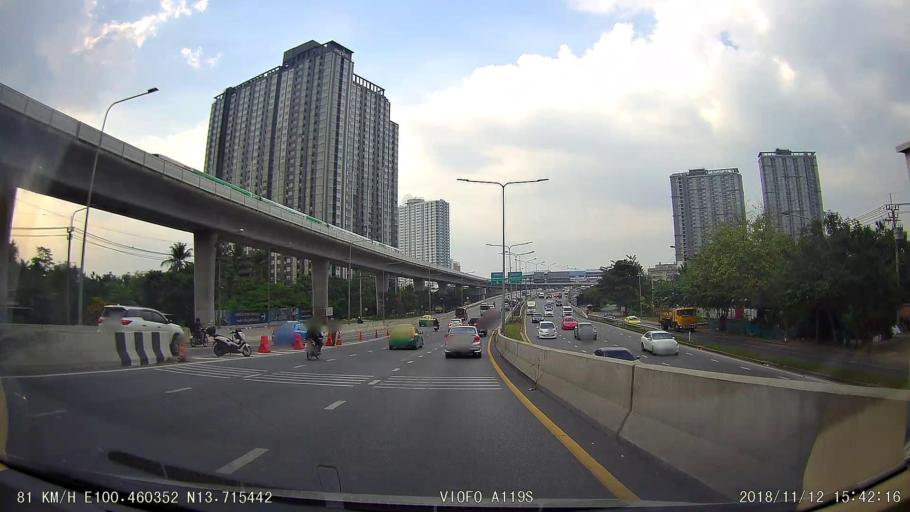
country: TH
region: Bangkok
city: Bangkok Yai
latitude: 13.7155
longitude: 100.4602
